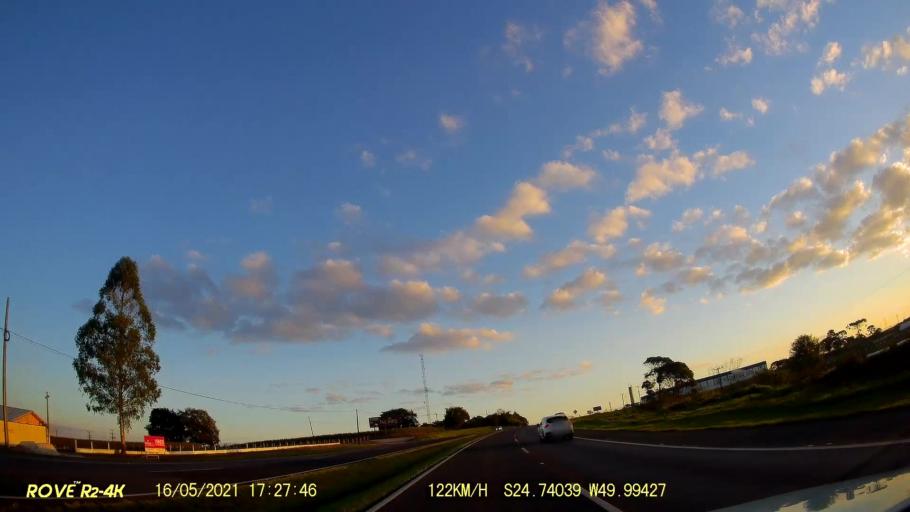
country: BR
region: Parana
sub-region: Castro
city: Castro
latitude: -24.7406
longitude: -49.9947
